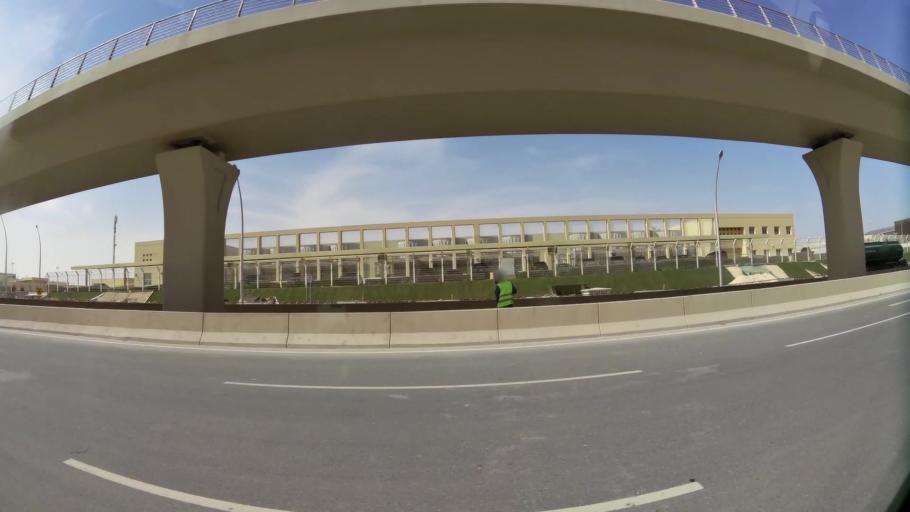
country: QA
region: Baladiyat ar Rayyan
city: Ar Rayyan
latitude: 25.3236
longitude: 51.4337
